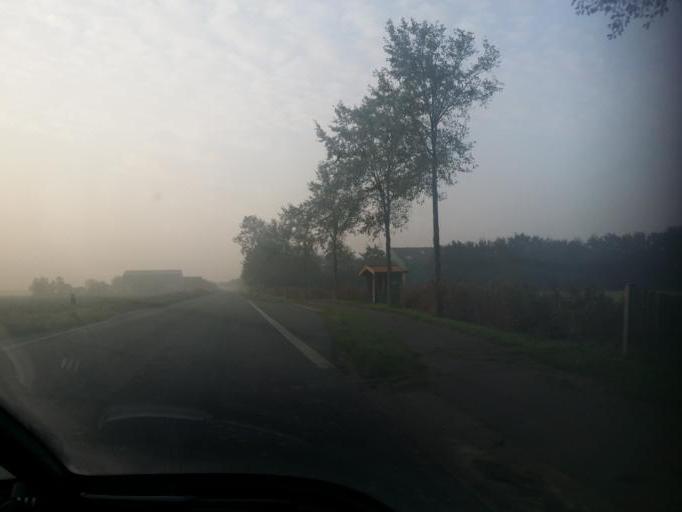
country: DE
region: Schleswig-Holstein
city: Elisabeth-Sophien-Koog
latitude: 54.5084
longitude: 8.9364
